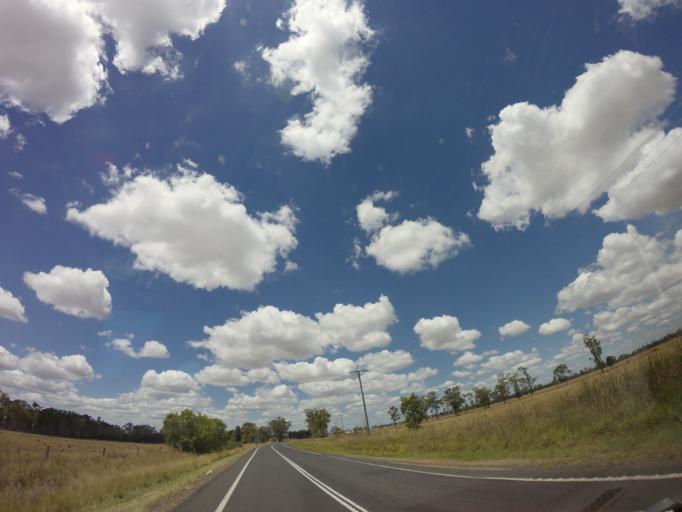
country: AU
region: Queensland
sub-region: Toowoomba
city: Oakey
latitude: -27.8750
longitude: 151.2364
